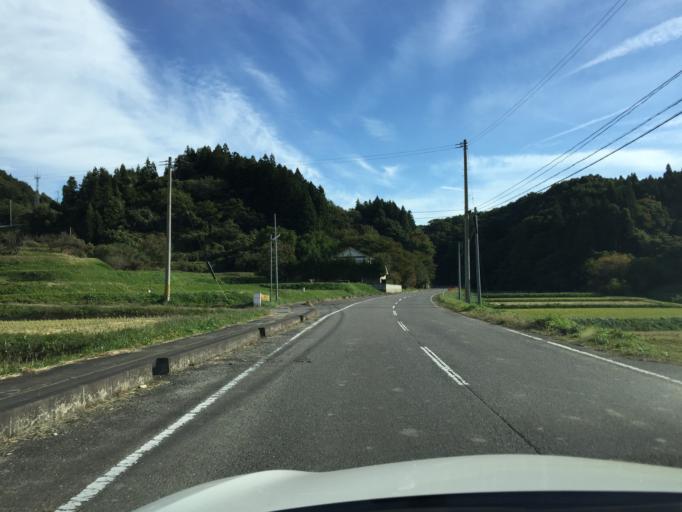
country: JP
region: Fukushima
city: Miharu
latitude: 37.3313
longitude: 140.4909
